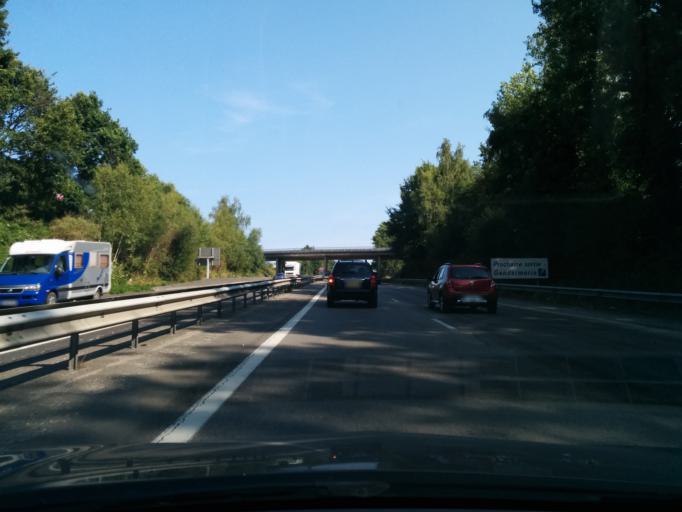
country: FR
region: Limousin
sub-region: Departement de la Haute-Vienne
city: Condat-sur-Vienne
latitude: 45.7959
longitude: 1.2985
